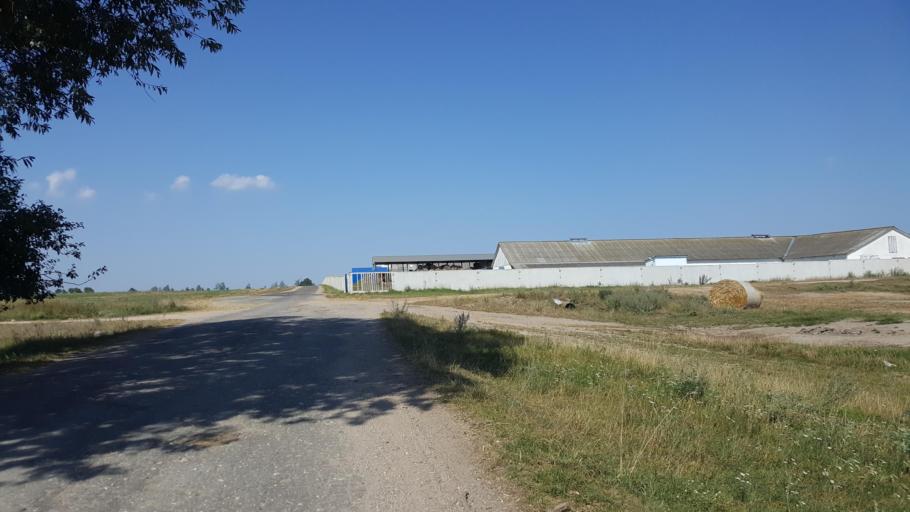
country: PL
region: Podlasie
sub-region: Powiat hajnowski
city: Czeremcha
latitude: 52.4797
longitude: 23.5490
